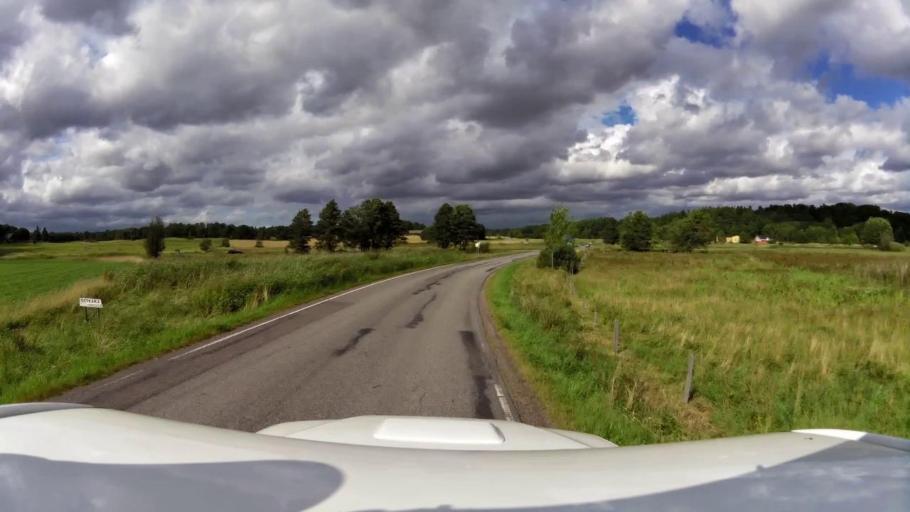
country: SE
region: OEstergoetland
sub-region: Linkopings Kommun
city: Sturefors
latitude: 58.3282
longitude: 15.7141
